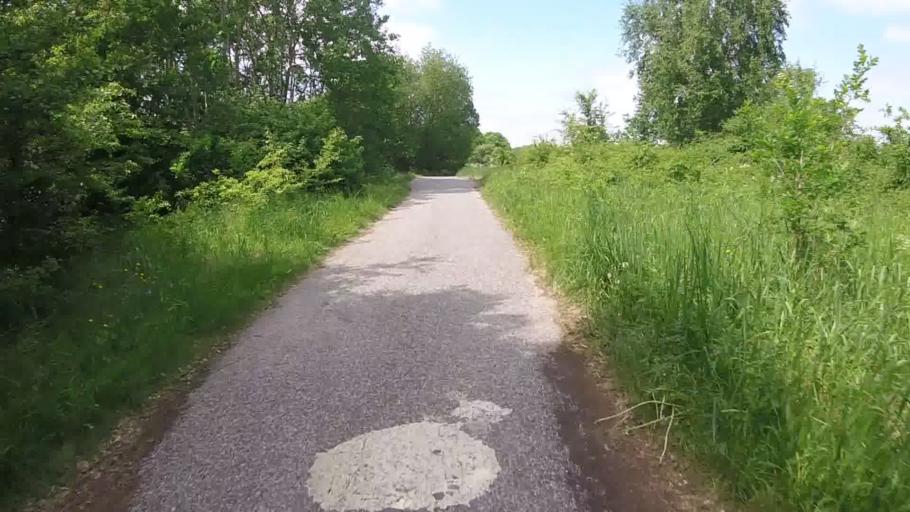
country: DE
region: Schleswig-Holstein
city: Oststeinbek
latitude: 53.4914
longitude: 10.1531
